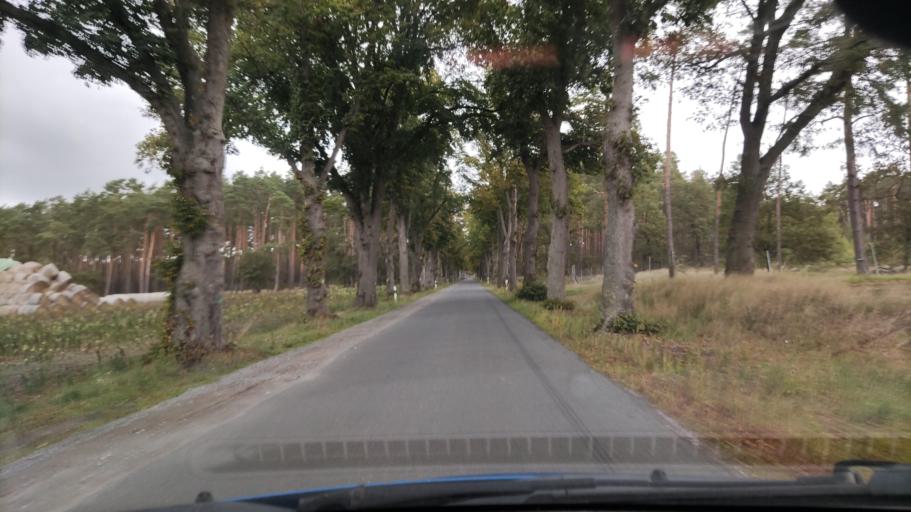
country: DE
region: Saxony-Anhalt
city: Luftkurort Arendsee
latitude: 52.9529
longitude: 11.5453
